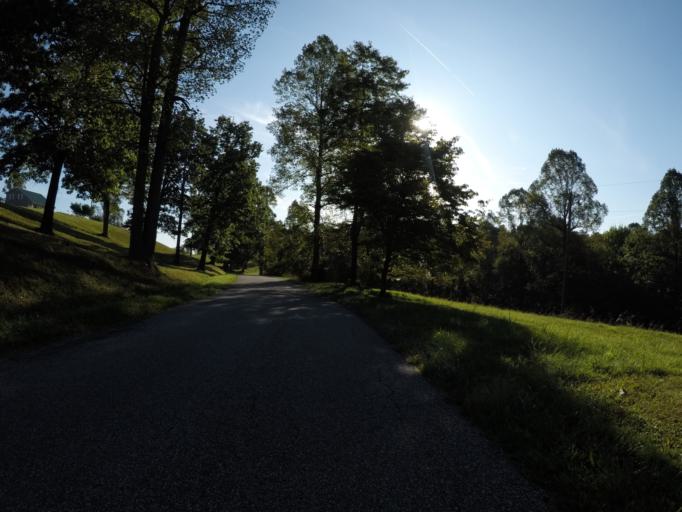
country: US
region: Ohio
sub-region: Lawrence County
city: Coal Grove
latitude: 38.5973
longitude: -82.5498
